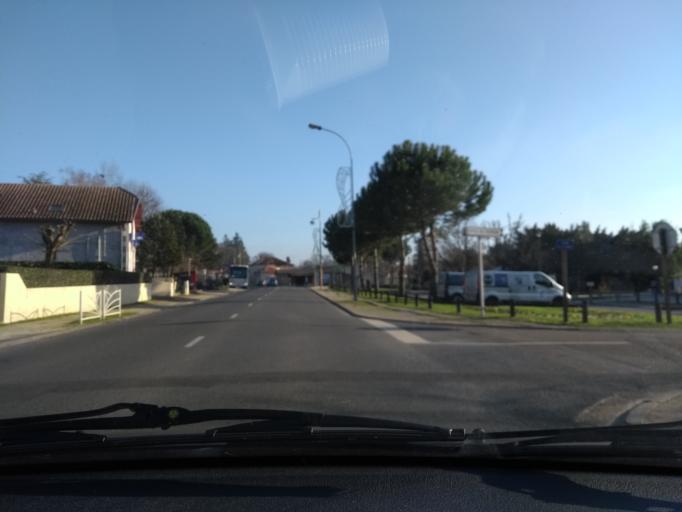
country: FR
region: Aquitaine
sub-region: Departement de la Gironde
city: Mios
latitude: 44.6067
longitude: -0.9402
